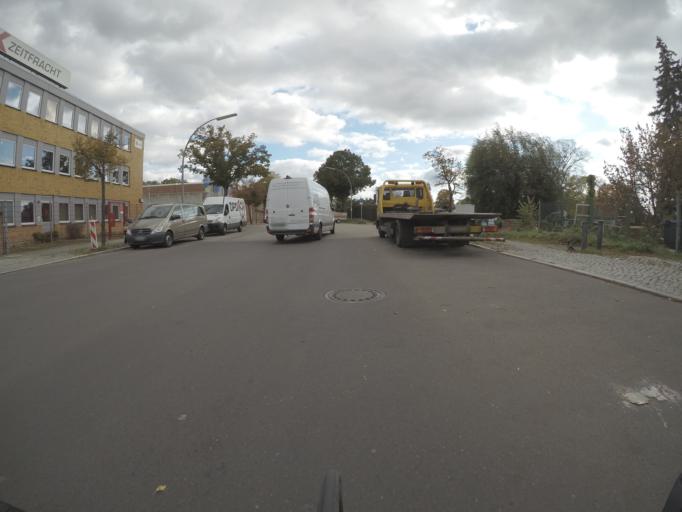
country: DE
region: Berlin
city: Charlottenburg-Nord
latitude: 52.5409
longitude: 13.3157
